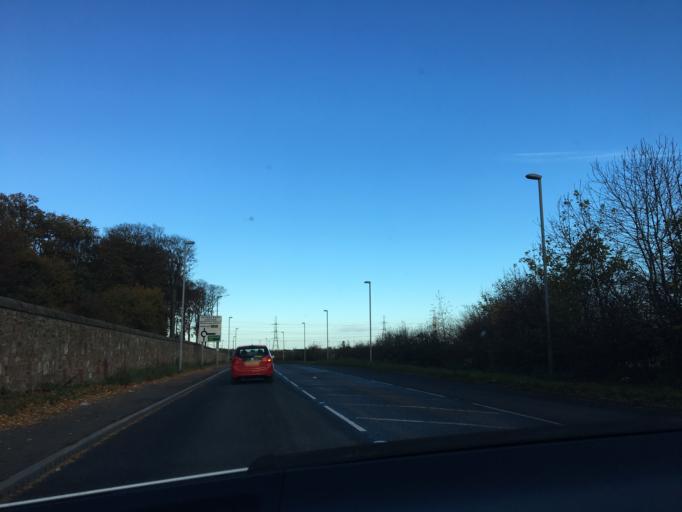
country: GB
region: Scotland
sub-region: Midlothian
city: Dalkeith
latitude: 55.9063
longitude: -3.0478
